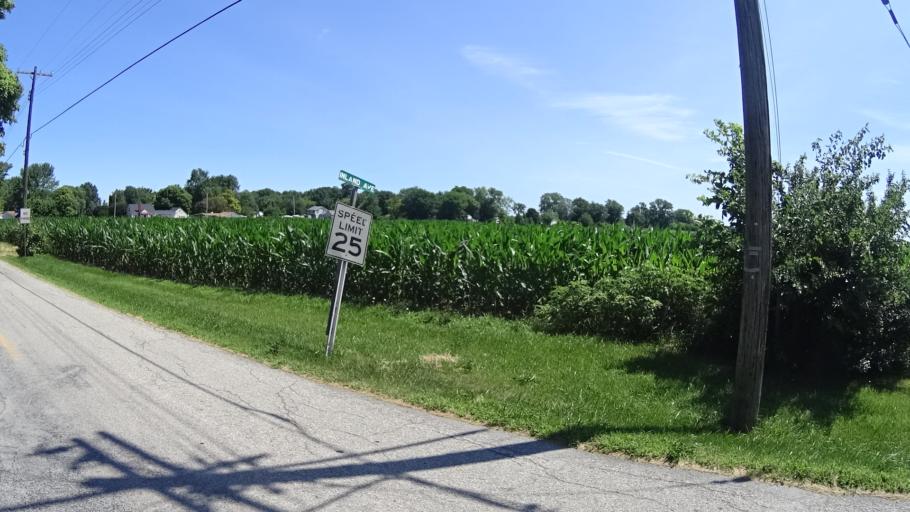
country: US
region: Ohio
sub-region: Ottawa County
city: Port Clinton
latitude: 41.4450
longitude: -82.8440
